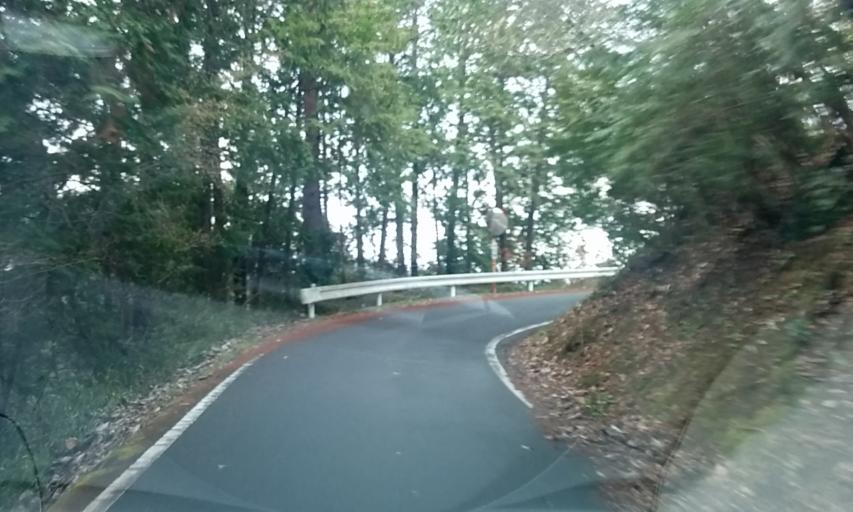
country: JP
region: Kyoto
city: Kameoka
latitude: 35.1136
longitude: 135.4299
